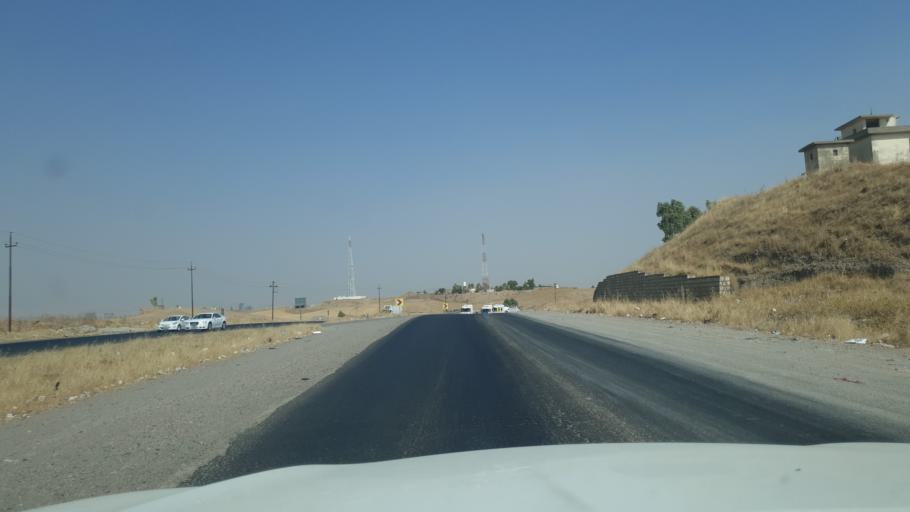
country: IQ
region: Arbil
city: Erbil
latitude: 36.1956
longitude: 43.8992
